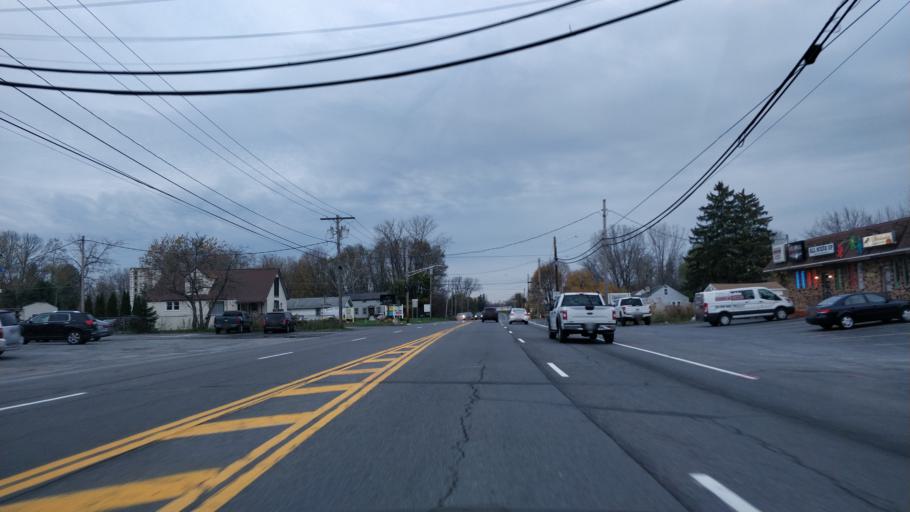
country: US
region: New York
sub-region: Onondaga County
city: North Syracuse
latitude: 43.1647
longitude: -76.1191
